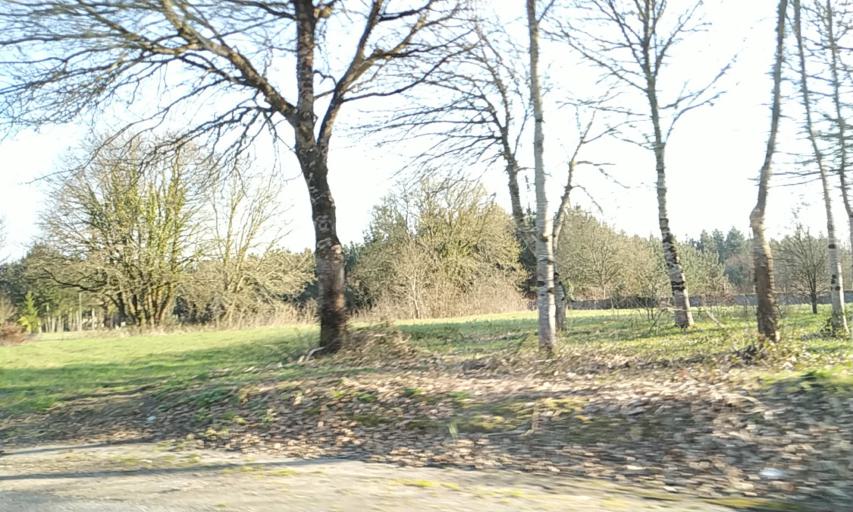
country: ES
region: Galicia
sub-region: Provincia de Lugo
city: Corgo
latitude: 42.9512
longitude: -7.4569
